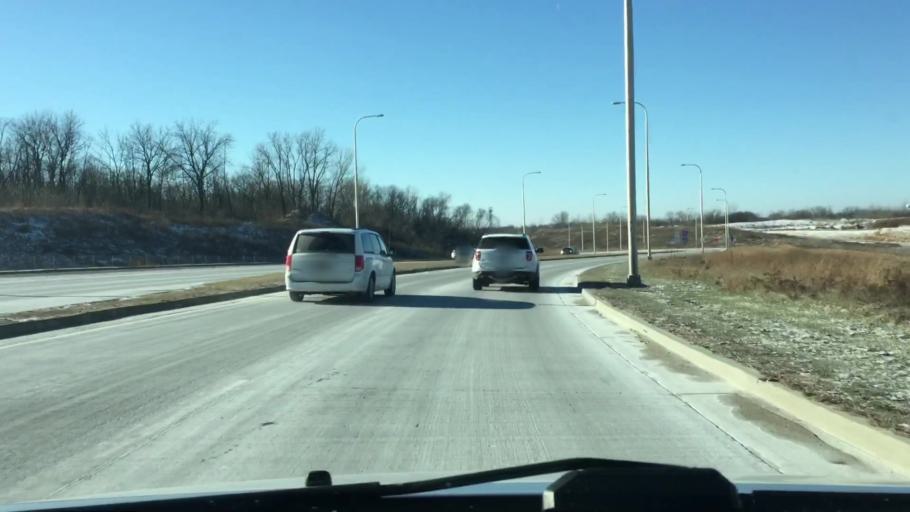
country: US
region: Illinois
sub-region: McHenry County
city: Algonquin
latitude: 42.1768
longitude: -88.2885
